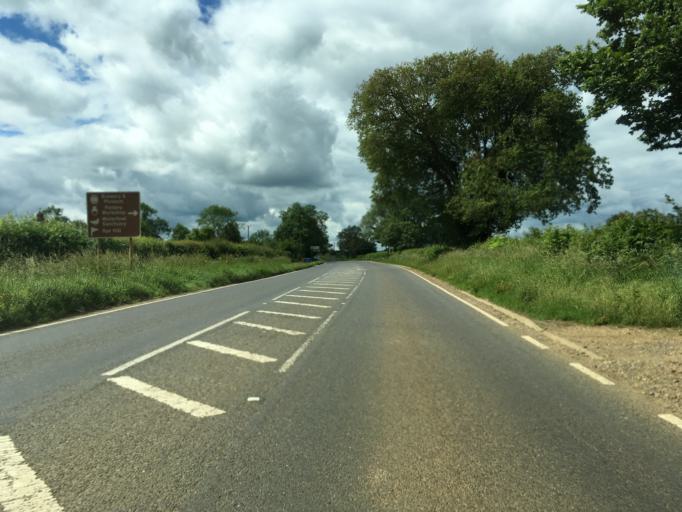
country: GB
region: England
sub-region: Oxfordshire
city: Bloxham
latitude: 52.0109
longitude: -1.3842
